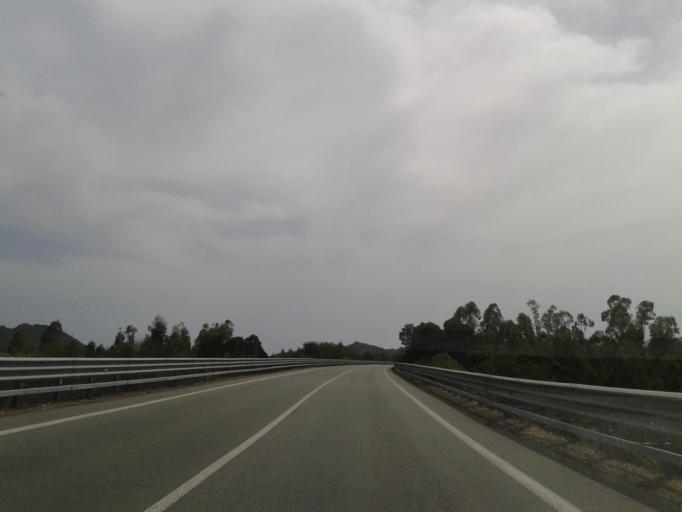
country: IT
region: Sardinia
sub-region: Provincia di Cagliari
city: Olia Speciosa
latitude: 39.2762
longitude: 9.5376
